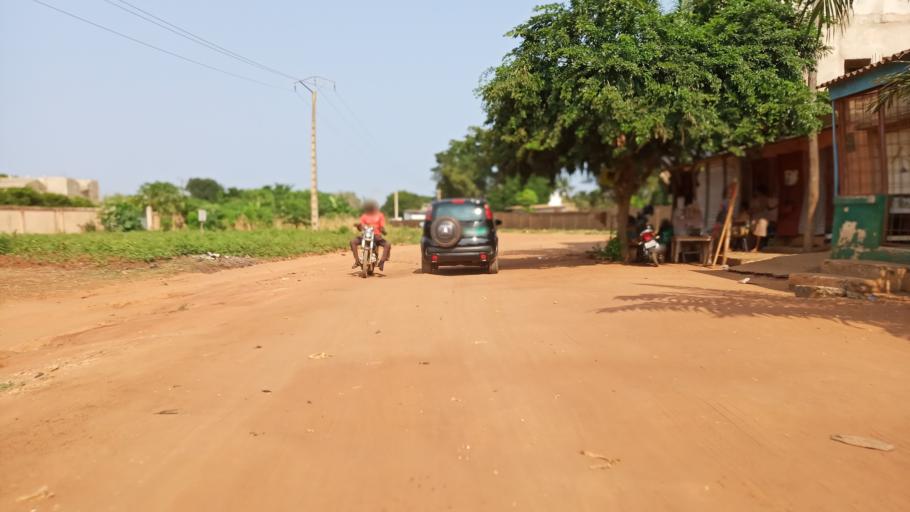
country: TG
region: Maritime
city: Lome
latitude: 6.2092
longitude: 1.2000
